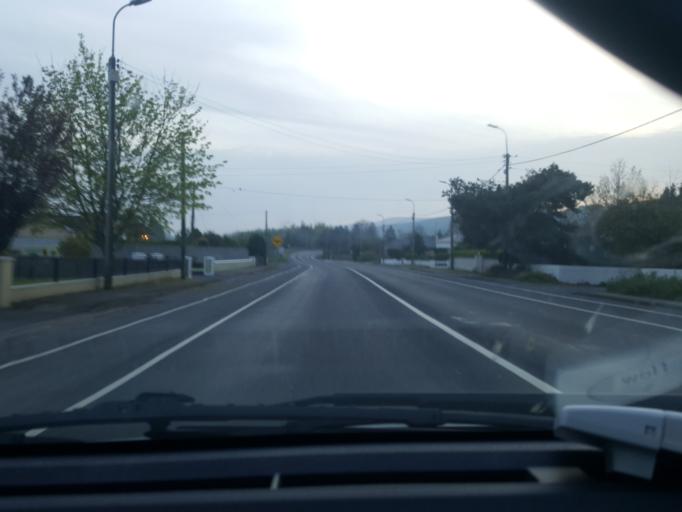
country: IE
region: Munster
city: Cahir
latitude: 52.3736
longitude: -7.9421
